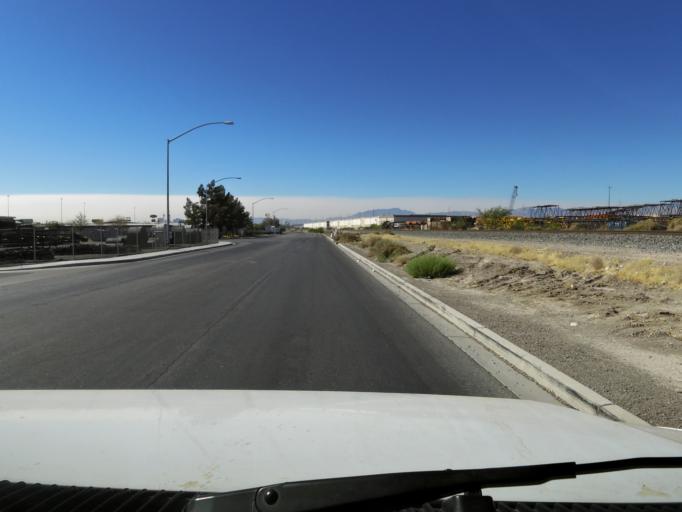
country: US
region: Nevada
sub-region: Clark County
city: North Las Vegas
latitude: 36.2386
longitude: -115.1085
